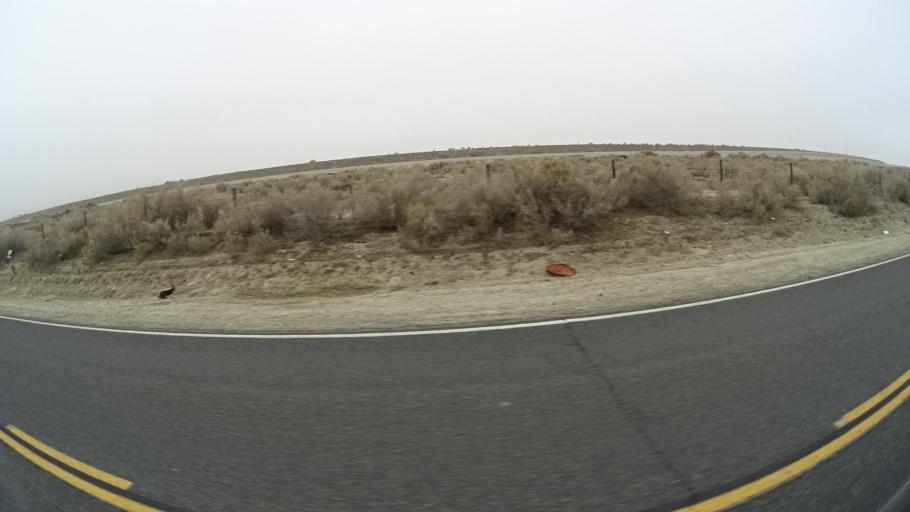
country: US
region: California
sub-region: Kern County
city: Buttonwillow
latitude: 35.3537
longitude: -119.4730
